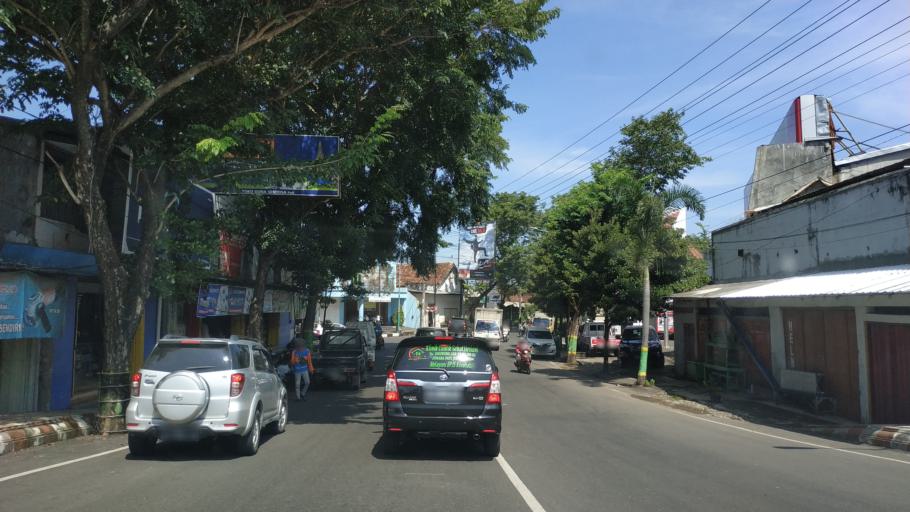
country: ID
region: Central Java
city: Baran
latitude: -6.7544
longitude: 111.0475
